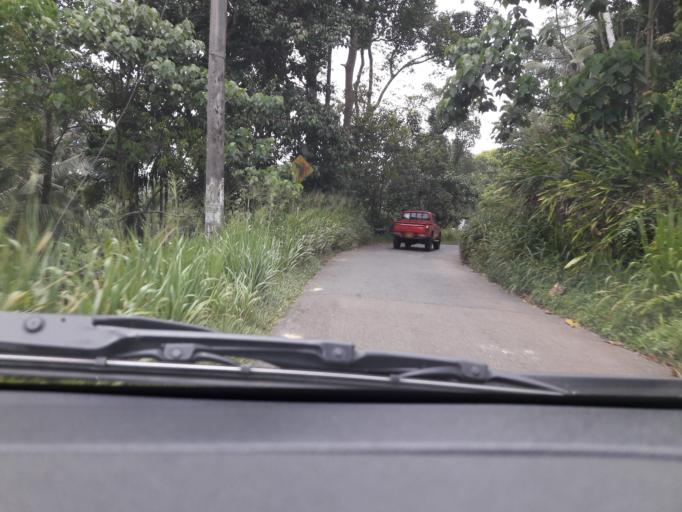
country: LK
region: Southern
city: Galle
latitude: 6.1982
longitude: 80.3015
